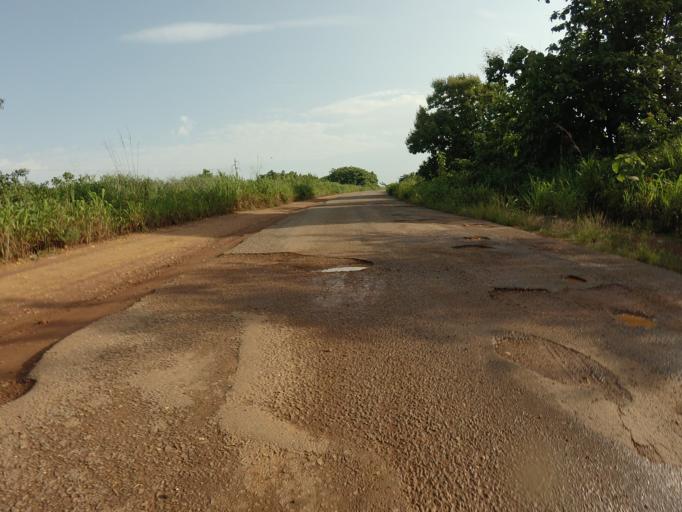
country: GH
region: Volta
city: Hohoe
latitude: 7.0839
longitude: 0.4441
